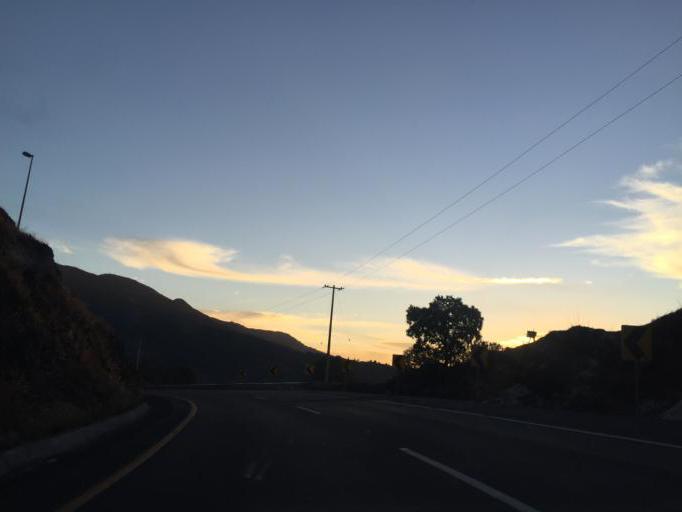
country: MX
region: Veracruz
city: Maltrata
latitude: 18.8505
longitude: -97.2732
